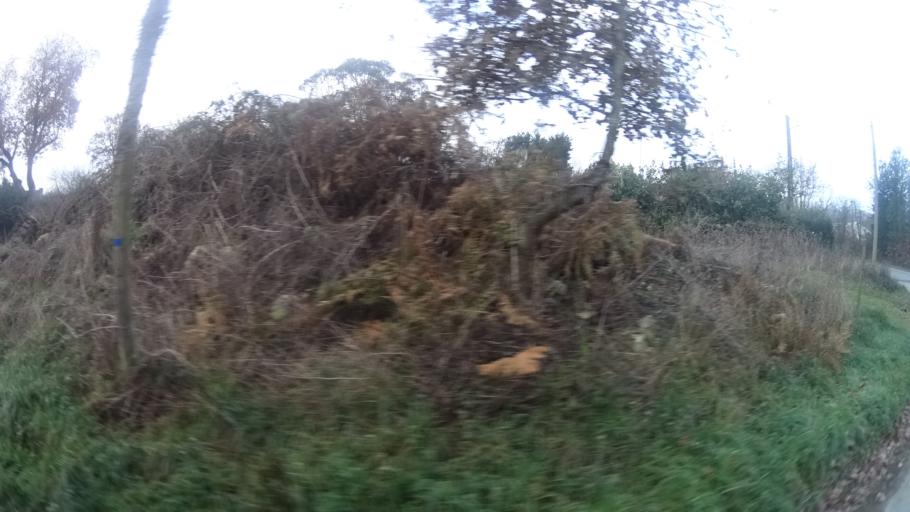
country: FR
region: Pays de la Loire
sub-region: Departement de la Loire-Atlantique
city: Saint-Nicolas-de-Redon
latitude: 47.6395
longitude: -2.0414
